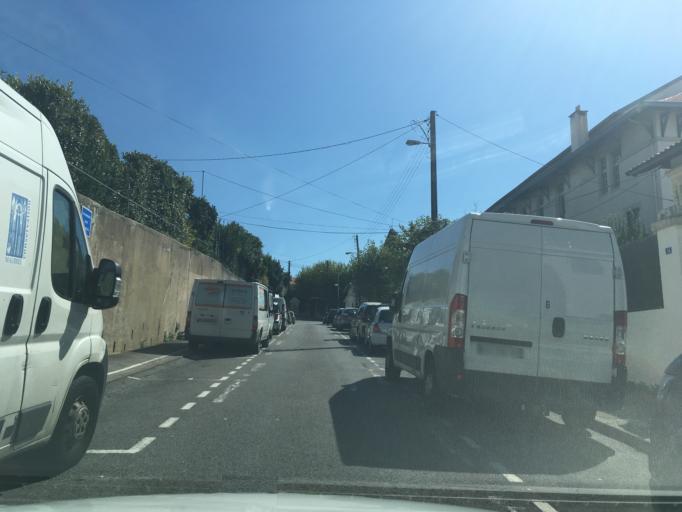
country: FR
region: Aquitaine
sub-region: Departement des Pyrenees-Atlantiques
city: Biarritz
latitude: 43.4806
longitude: -1.5535
